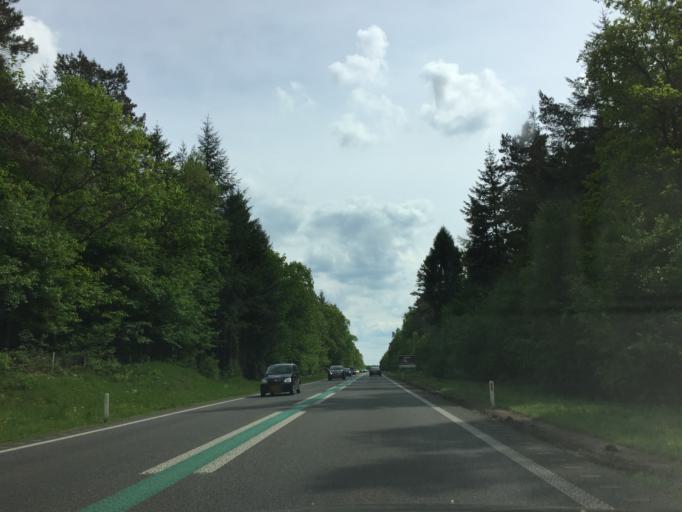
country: NL
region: Drenthe
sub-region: Gemeente Borger-Odoorn
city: Borger
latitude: 52.9596
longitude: 6.7807
